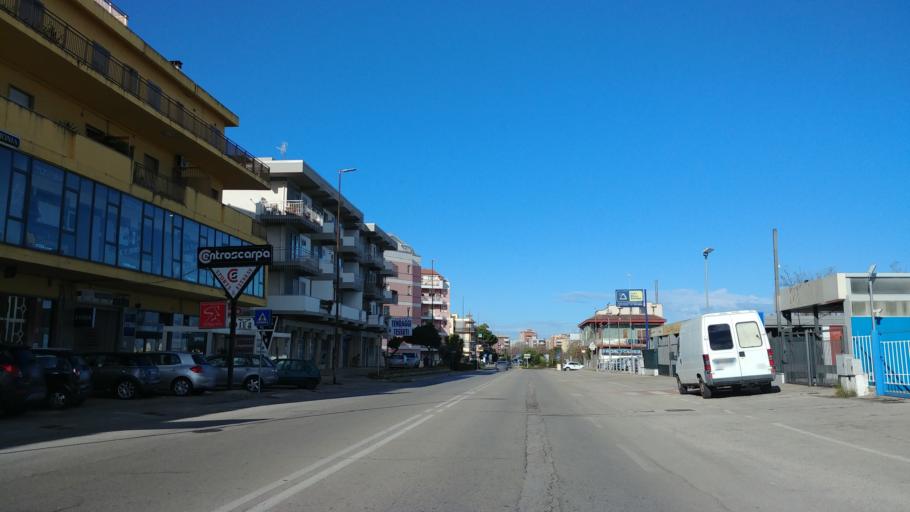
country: IT
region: Molise
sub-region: Provincia di Campobasso
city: Termoli
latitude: 41.9919
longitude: 14.9994
